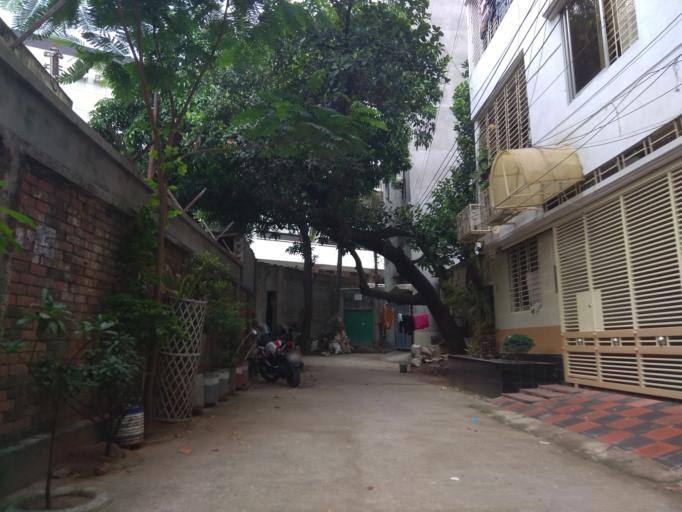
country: BD
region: Dhaka
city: Azimpur
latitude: 23.8074
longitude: 90.3650
